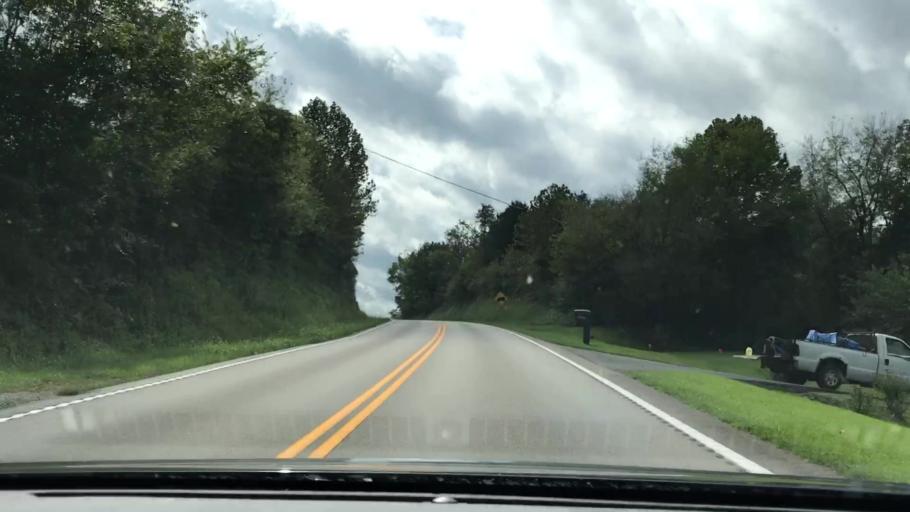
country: US
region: Kentucky
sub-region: Cumberland County
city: Burkesville
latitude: 36.8037
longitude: -85.4253
